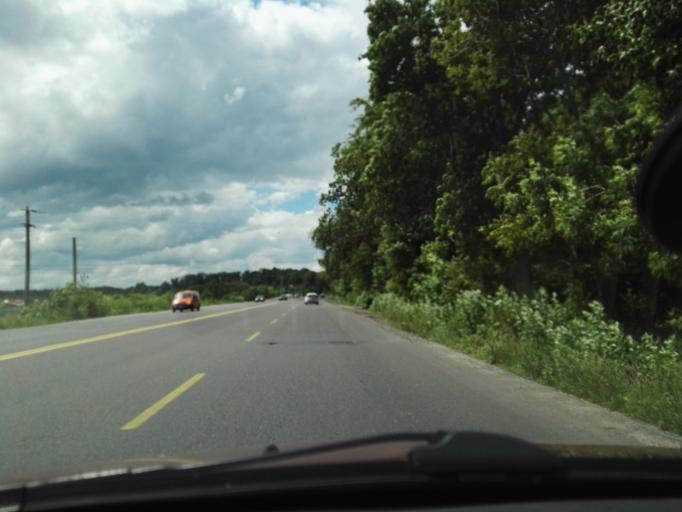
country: RO
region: Ilfov
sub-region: Comuna Jilava
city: Jilava
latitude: 44.3204
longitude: 26.0695
